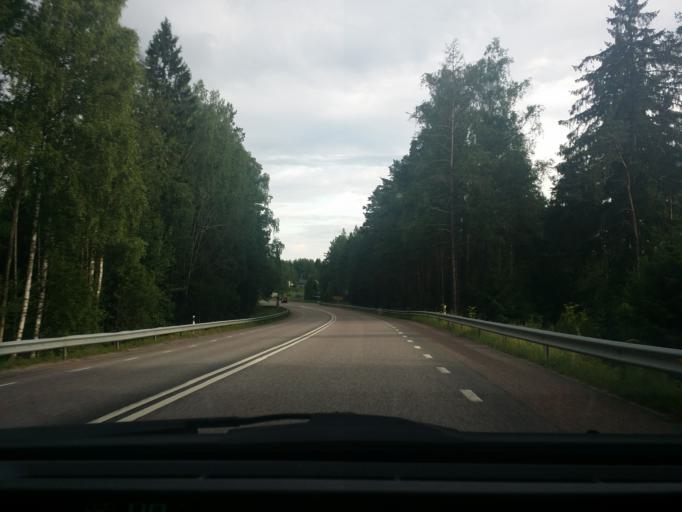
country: SE
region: OErebro
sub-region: Orebro Kommun
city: Hovsta
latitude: 59.4450
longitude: 15.1399
